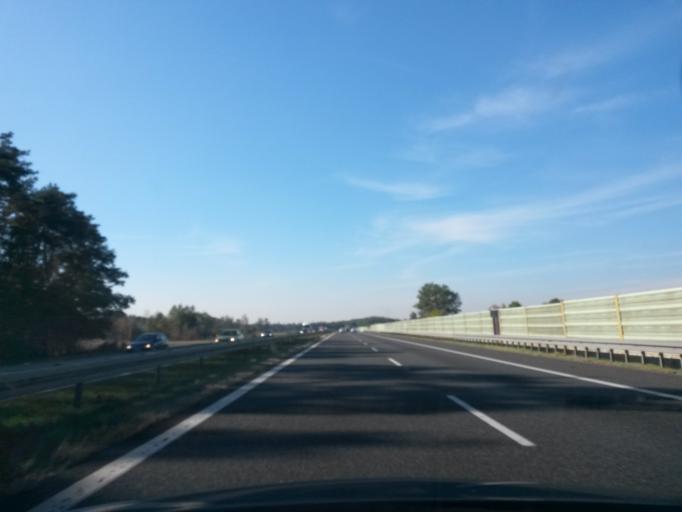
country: PL
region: Silesian Voivodeship
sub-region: Powiat gliwicki
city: Rudziniec
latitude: 50.3769
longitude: 18.4759
